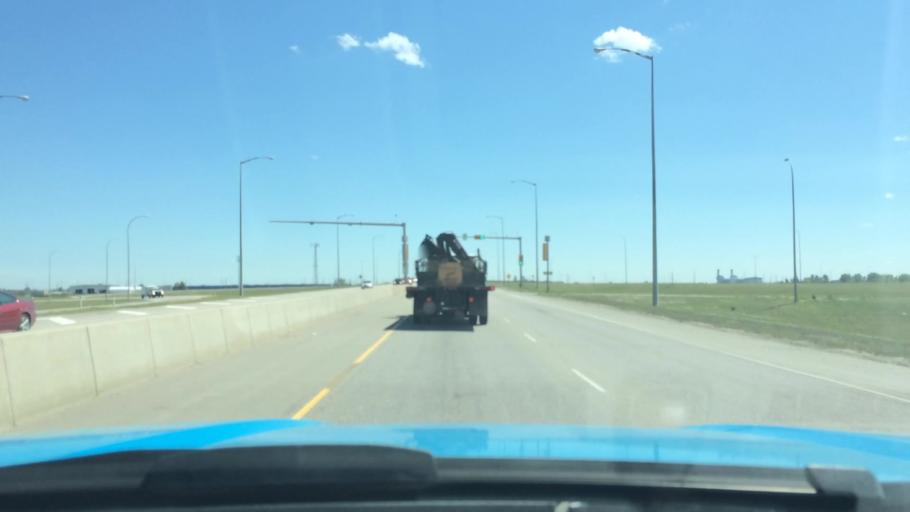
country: CA
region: Alberta
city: Chestermere
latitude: 50.9795
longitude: -113.9261
